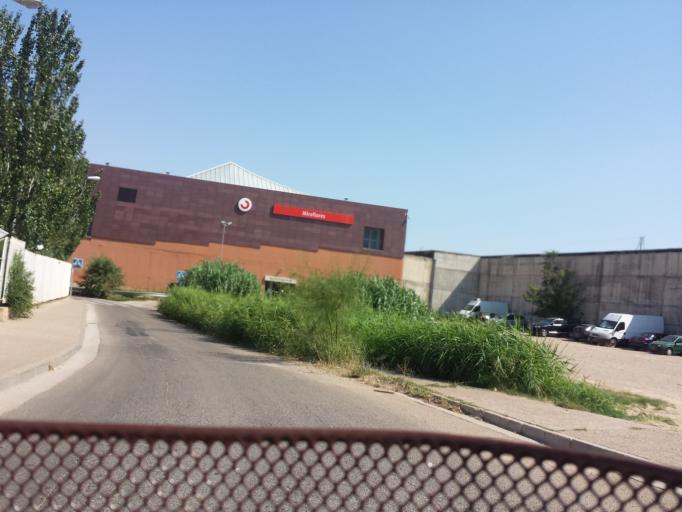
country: ES
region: Aragon
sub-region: Provincia de Zaragoza
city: Zaragoza
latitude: 41.6340
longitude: -0.8688
